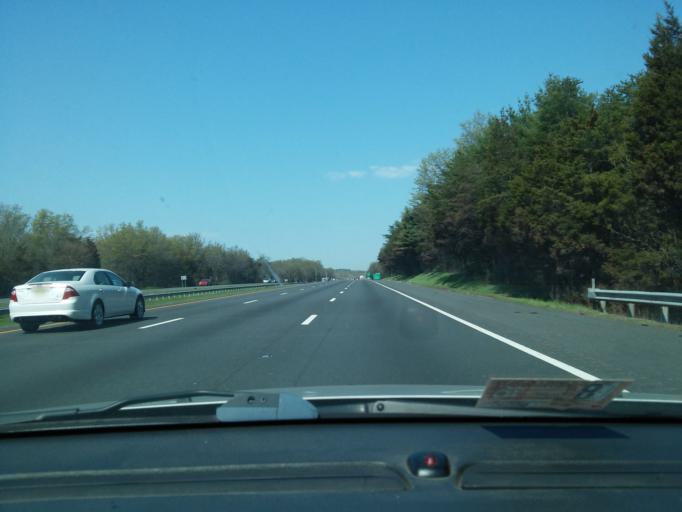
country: US
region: New Jersey
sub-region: Somerset County
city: Bedminster
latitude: 40.6438
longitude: -74.7023
